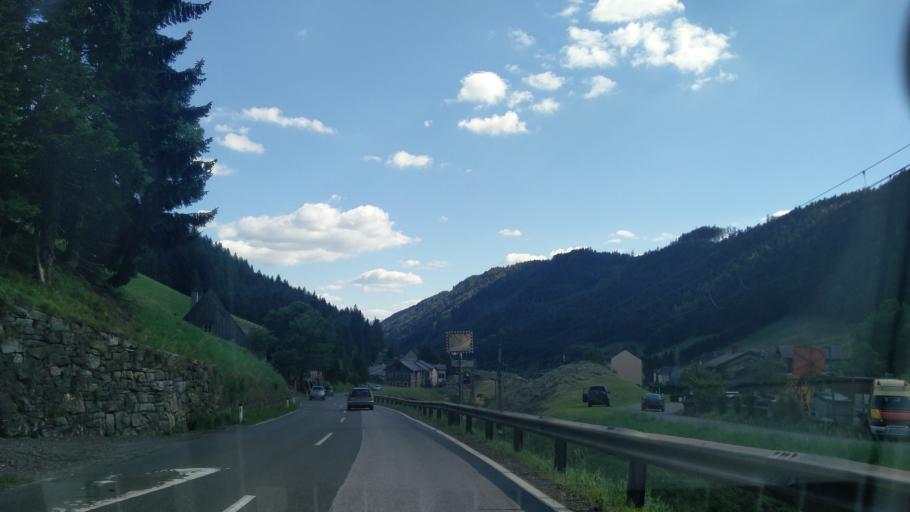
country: AT
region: Styria
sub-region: Politischer Bezirk Leoben
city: Vordernberg
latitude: 47.4747
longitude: 14.9878
